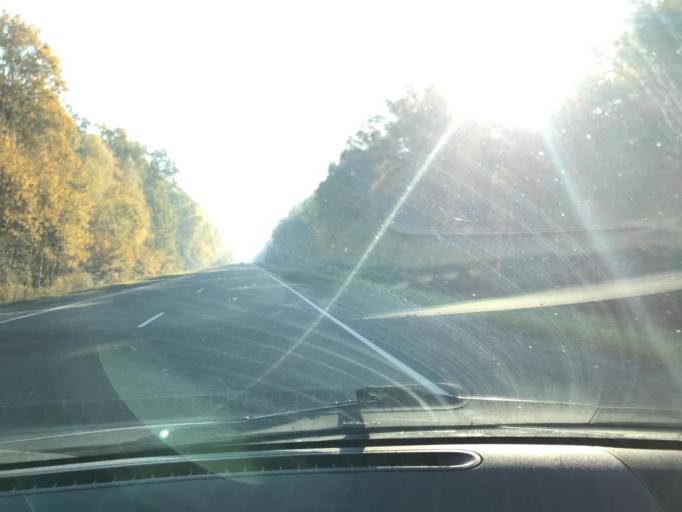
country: BY
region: Brest
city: Horad Luninyets
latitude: 52.3094
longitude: 26.6763
